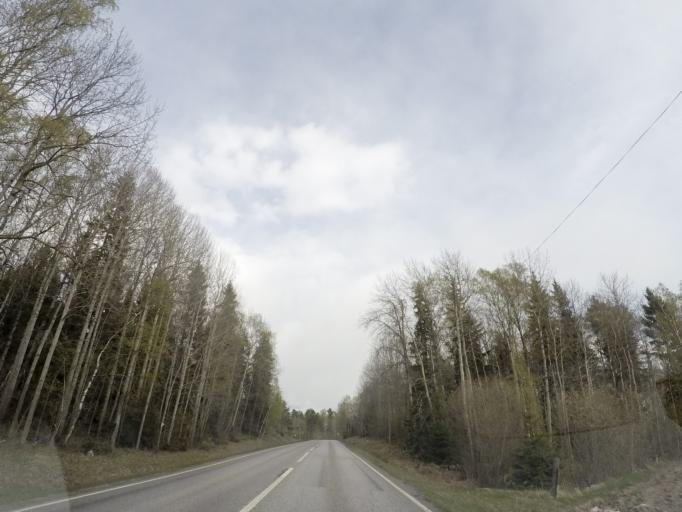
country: SE
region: Vaestmanland
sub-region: Kungsors Kommun
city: Kungsoer
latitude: 59.2850
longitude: 16.1480
